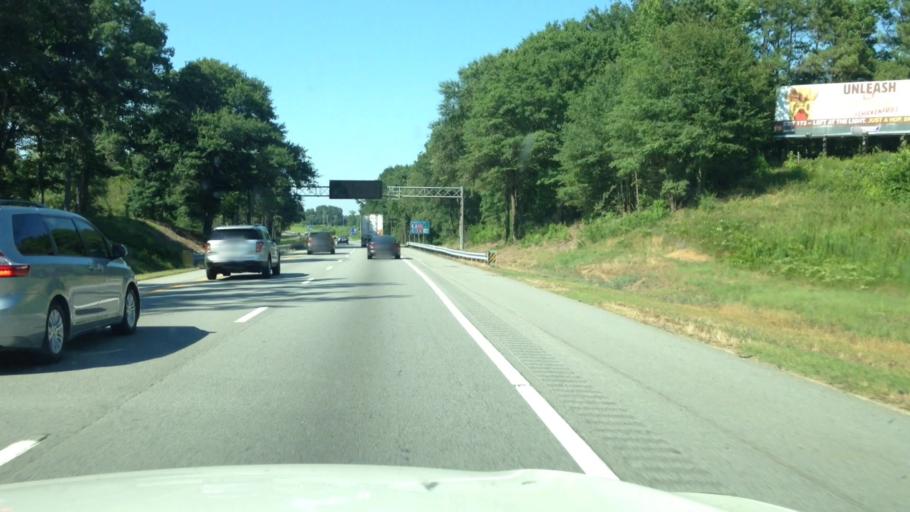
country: US
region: North Carolina
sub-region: Halifax County
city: Weldon
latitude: 36.4160
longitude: -77.6348
